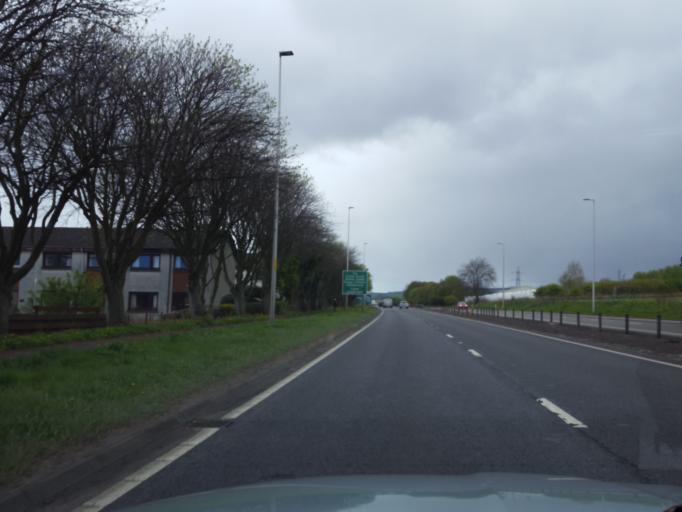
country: GB
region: Scotland
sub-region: Angus
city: Muirhead
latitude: 56.4589
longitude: -3.1158
